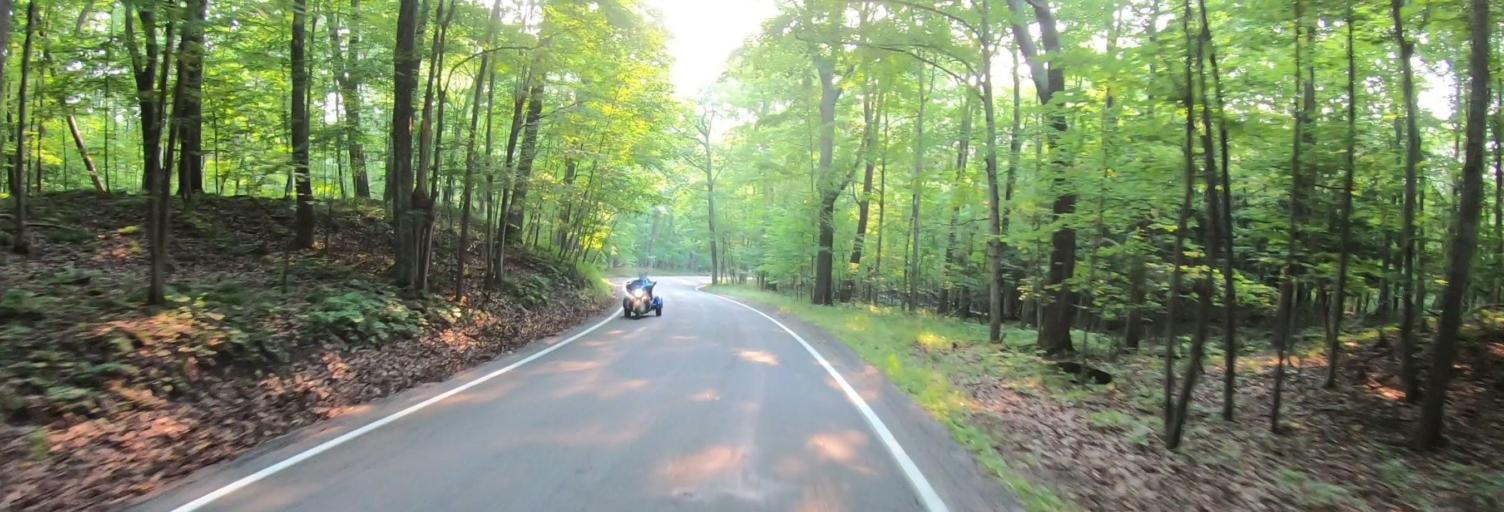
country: US
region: Michigan
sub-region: Emmet County
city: Harbor Springs
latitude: 45.4886
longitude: -85.0881
